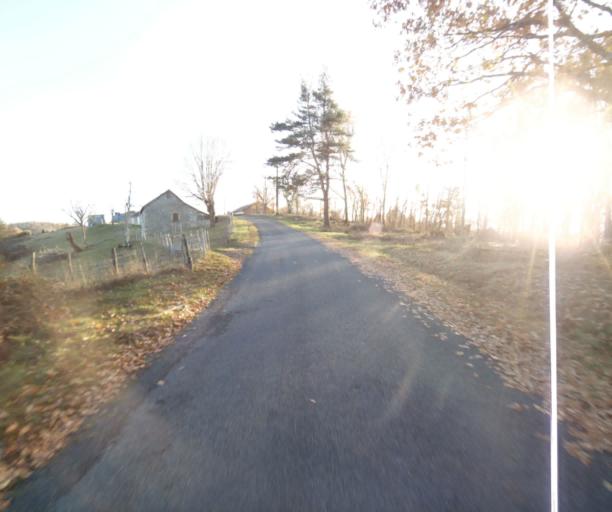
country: FR
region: Limousin
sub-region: Departement de la Correze
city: Laguenne
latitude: 45.2308
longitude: 1.8009
